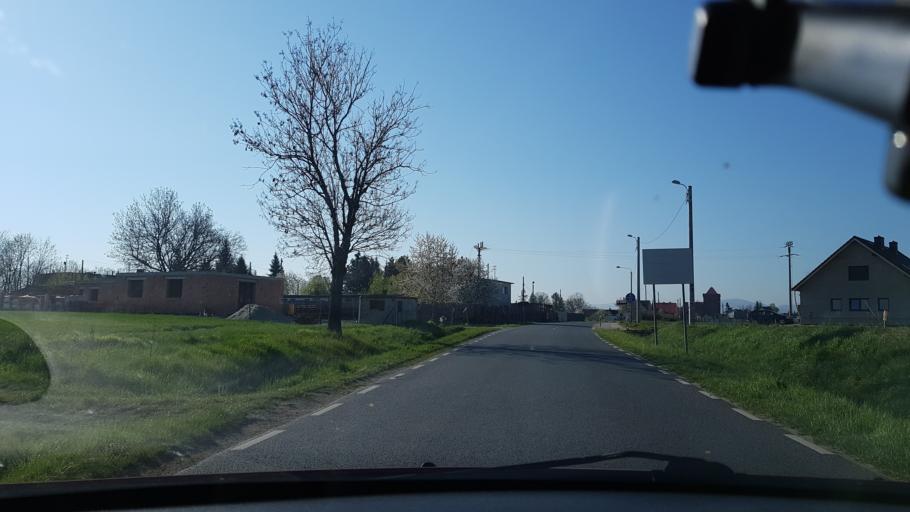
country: CZ
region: Olomoucky
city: Vidnava
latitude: 50.4104
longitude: 17.1867
